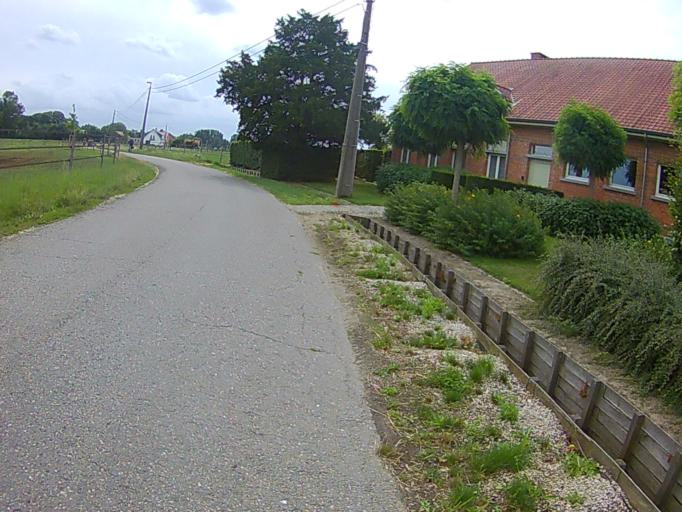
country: BE
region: Flanders
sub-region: Provincie Antwerpen
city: Zandhoven
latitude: 51.1821
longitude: 4.6259
